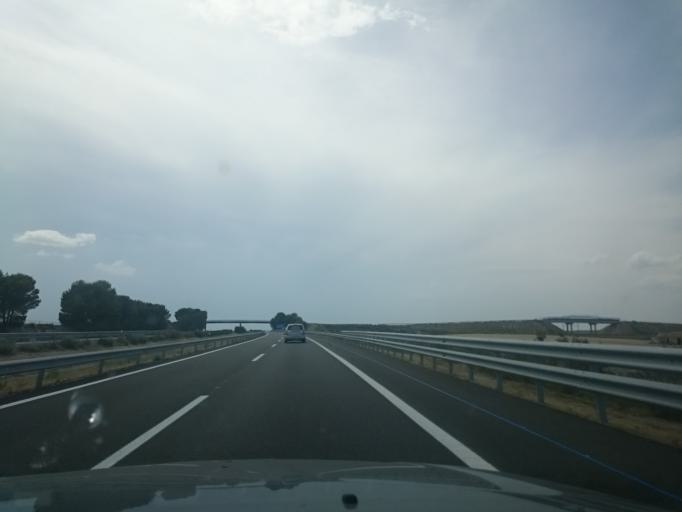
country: ES
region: Aragon
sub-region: Provincia de Zaragoza
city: Bujaraloz
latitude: 41.5263
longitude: -0.1915
